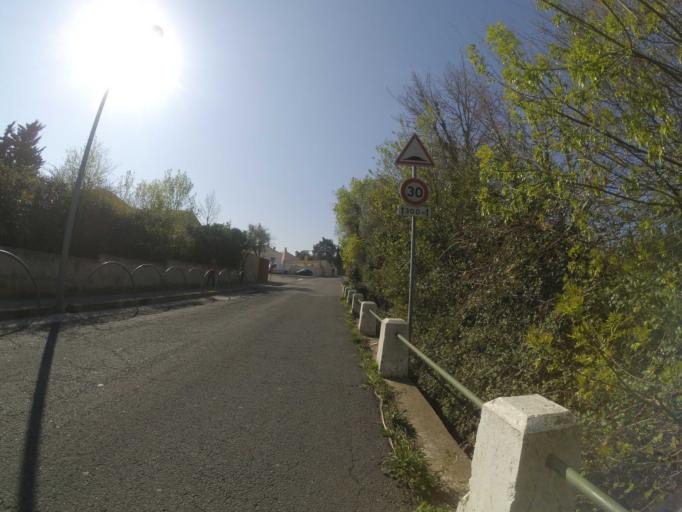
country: FR
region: Languedoc-Roussillon
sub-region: Departement des Pyrenees-Orientales
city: Thuir
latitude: 42.6260
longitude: 2.7508
